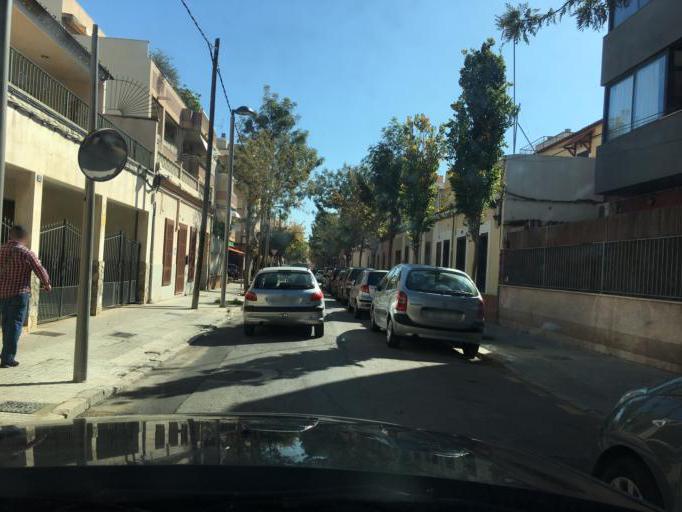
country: ES
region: Balearic Islands
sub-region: Illes Balears
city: Palma
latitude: 39.5852
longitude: 2.6748
